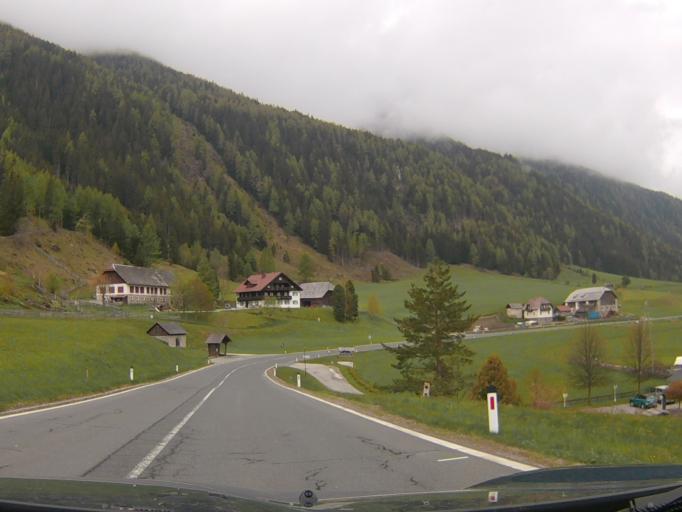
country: AT
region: Carinthia
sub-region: Politischer Bezirk Spittal an der Drau
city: Obervellach
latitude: 46.9734
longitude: 13.1791
